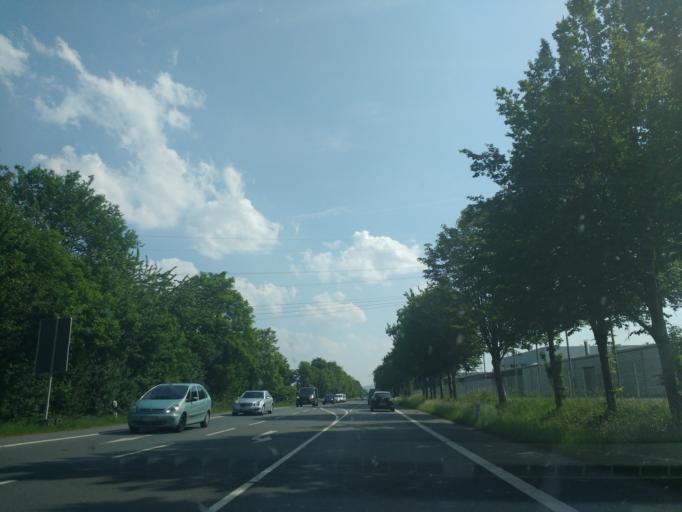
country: DE
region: North Rhine-Westphalia
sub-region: Regierungsbezirk Detmold
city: Bad Salzuflen
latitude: 52.0491
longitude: 8.7589
